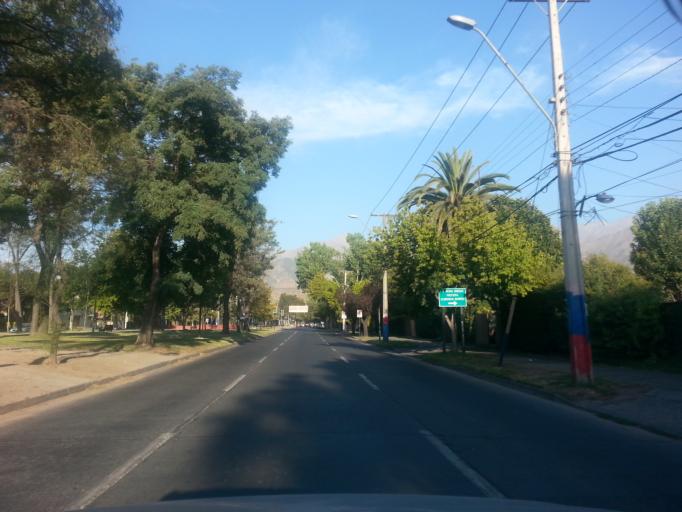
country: CL
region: Santiago Metropolitan
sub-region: Provincia de Santiago
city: Villa Presidente Frei, Nunoa, Santiago, Chile
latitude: -33.4306
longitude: -70.5530
